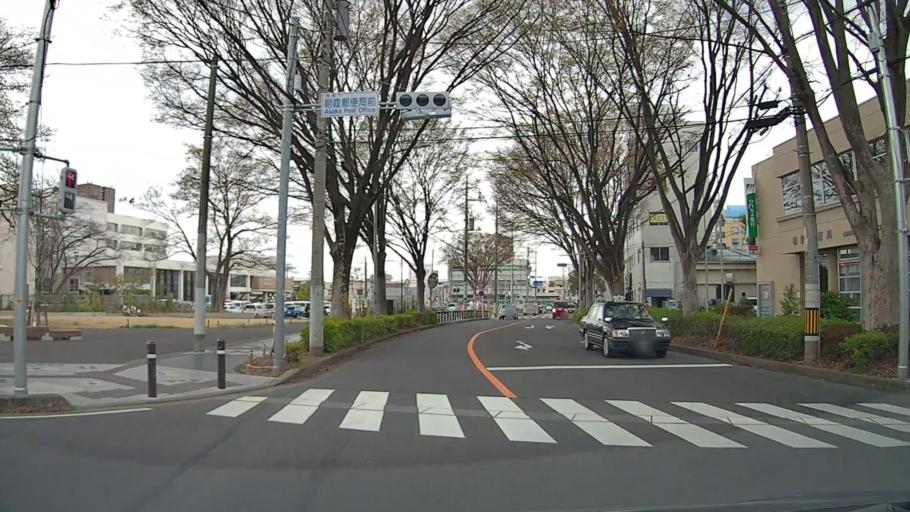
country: JP
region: Saitama
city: Asaka
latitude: 35.7959
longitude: 139.5945
